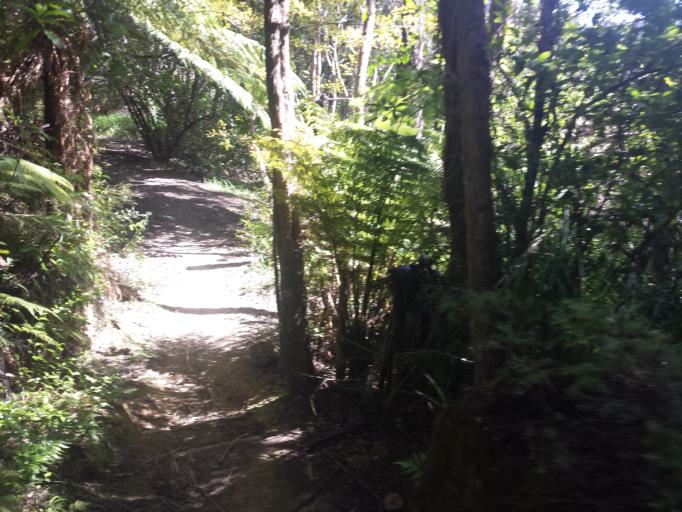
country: NZ
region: Northland
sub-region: Far North District
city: Paihia
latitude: -35.3035
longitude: 174.1055
